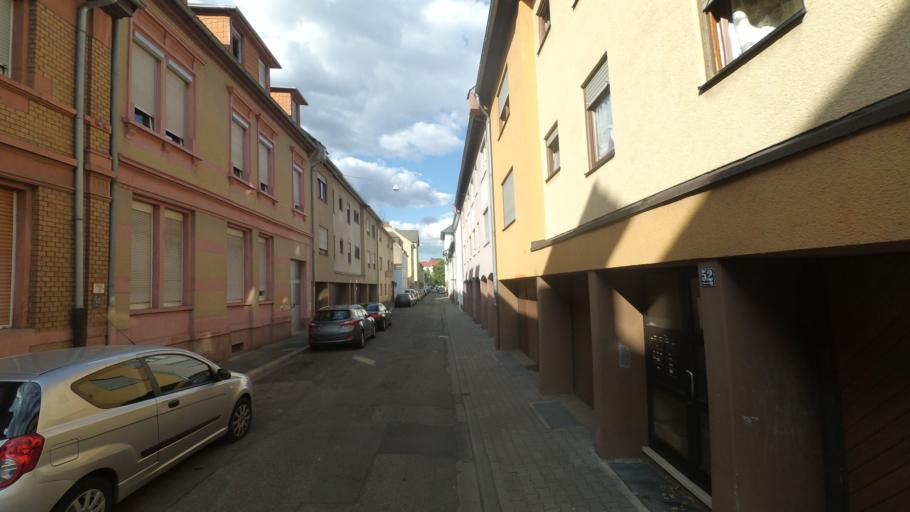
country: DE
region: Baden-Wuerttemberg
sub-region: Karlsruhe Region
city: Mannheim
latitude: 49.5029
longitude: 8.4652
